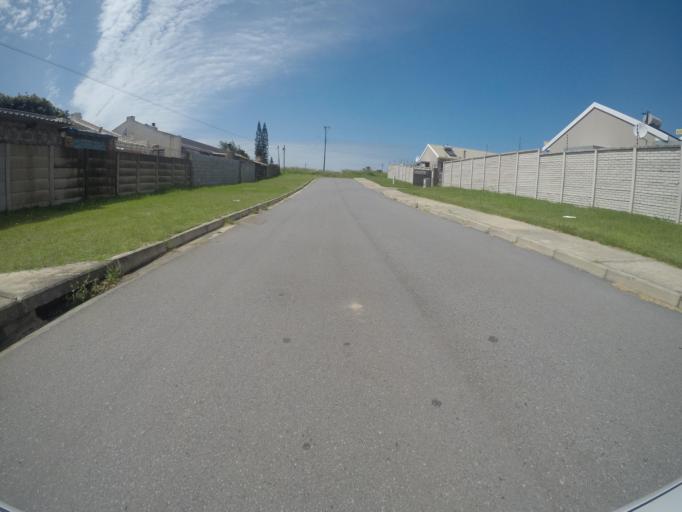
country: ZA
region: Eastern Cape
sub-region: Buffalo City Metropolitan Municipality
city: East London
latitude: -32.9533
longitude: 27.9967
